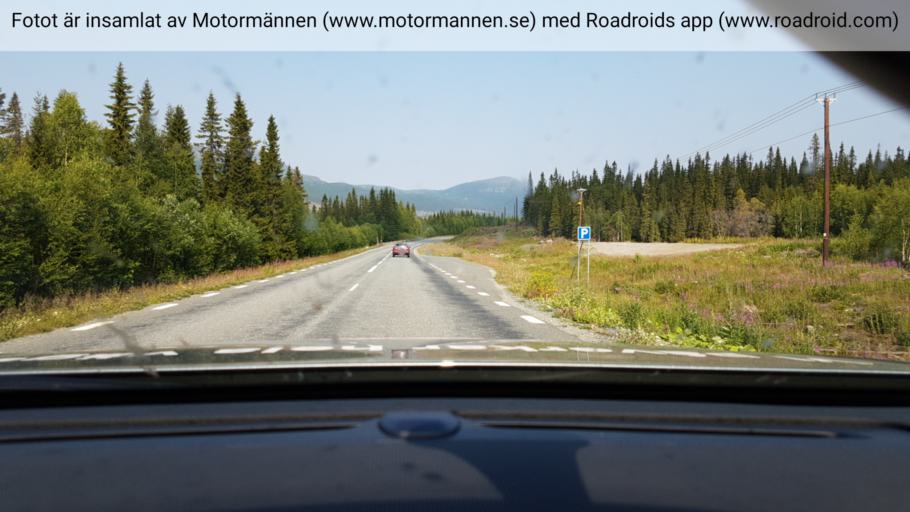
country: SE
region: Vaesterbotten
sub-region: Vilhelmina Kommun
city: Sjoberg
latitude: 65.5982
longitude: 15.5279
